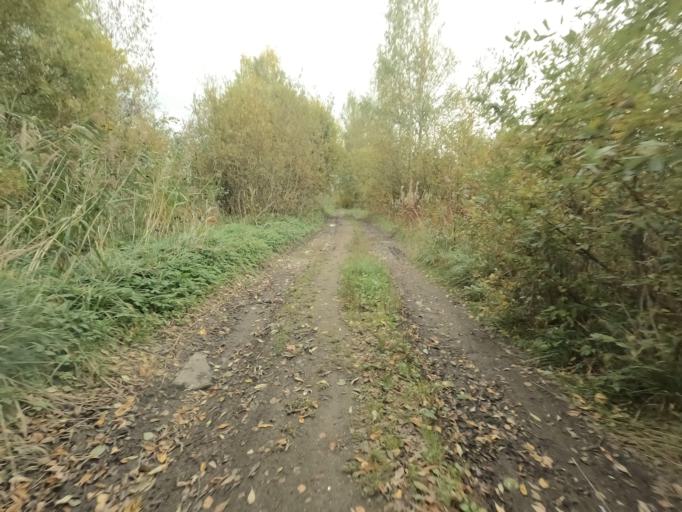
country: RU
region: St.-Petersburg
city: Sapernyy
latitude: 59.7784
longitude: 30.6390
